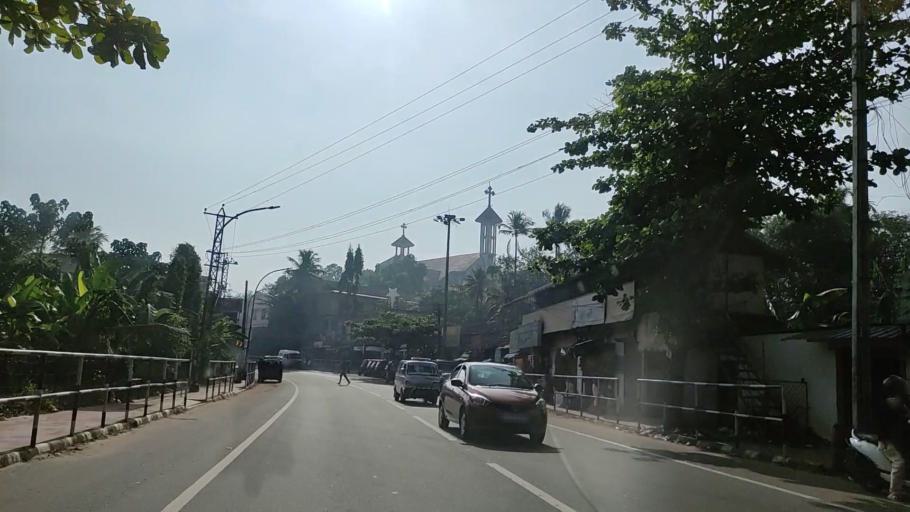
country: IN
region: Kerala
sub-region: Kollam
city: Punalur
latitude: 8.9731
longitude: 76.8229
